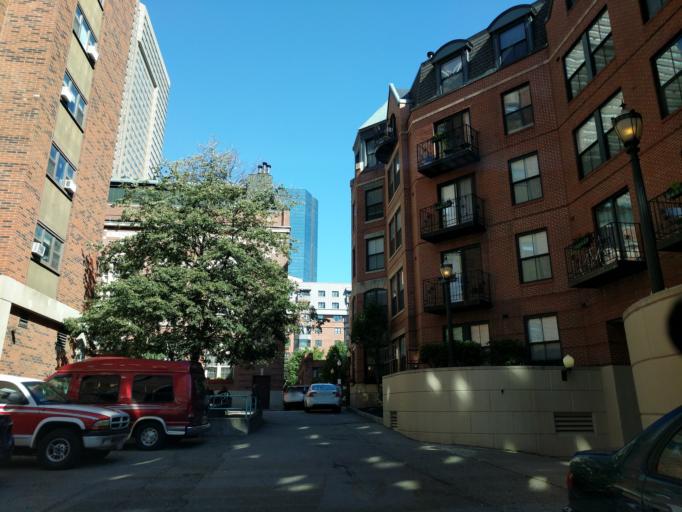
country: US
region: Massachusetts
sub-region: Suffolk County
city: Boston
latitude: 42.3454
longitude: -71.0796
